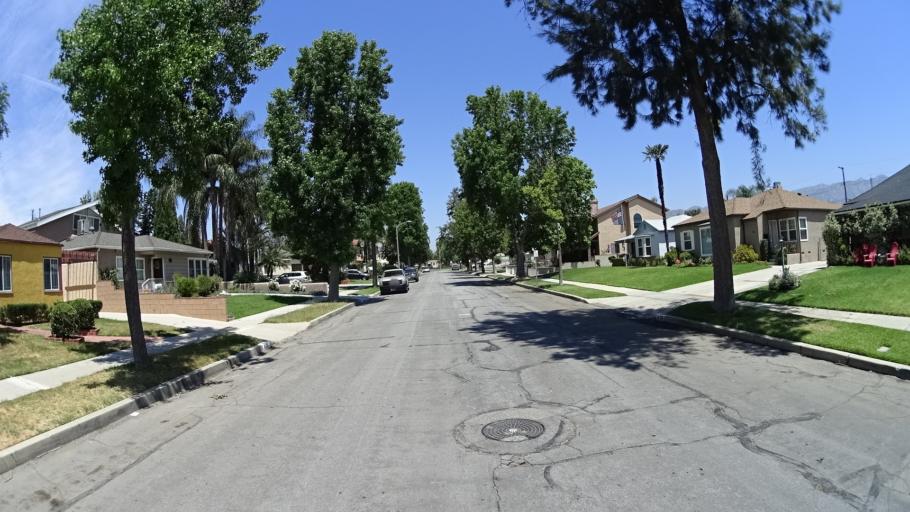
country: US
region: California
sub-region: Los Angeles County
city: Burbank
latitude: 34.1779
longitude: -118.3246
